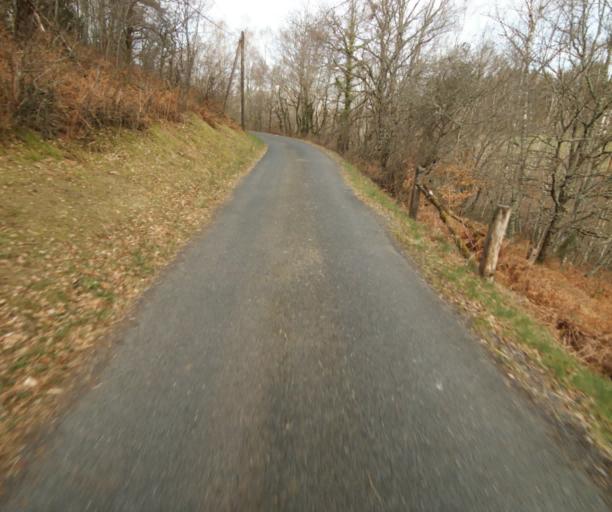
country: FR
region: Limousin
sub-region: Departement de la Correze
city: Treignac
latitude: 45.4700
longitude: 1.8250
